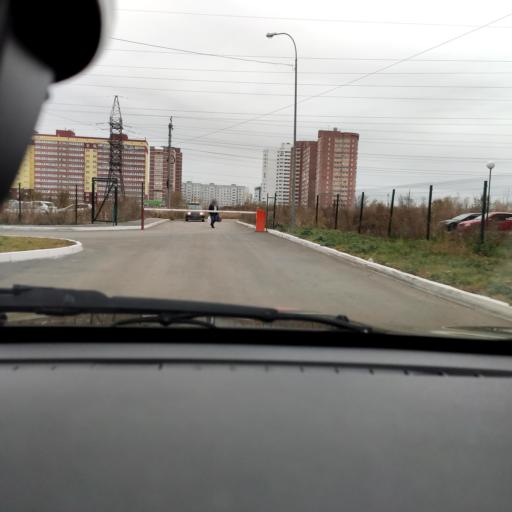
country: RU
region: Samara
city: Tol'yatti
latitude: 53.5446
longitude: 49.3968
